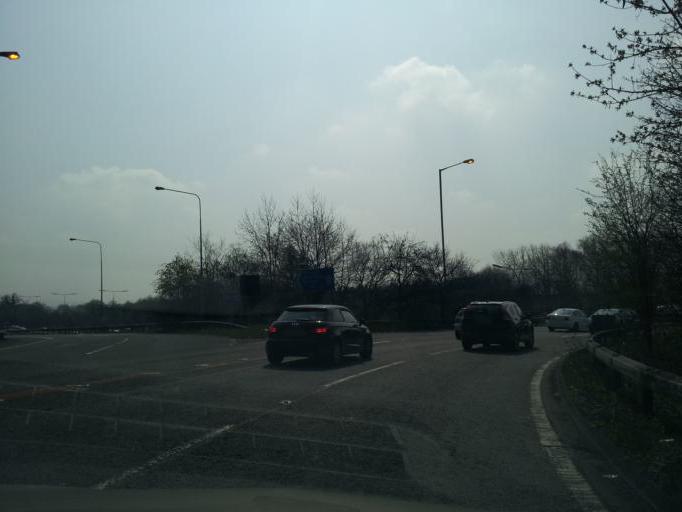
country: GB
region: England
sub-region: Hertfordshire
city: Bushey
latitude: 51.6719
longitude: -0.3679
